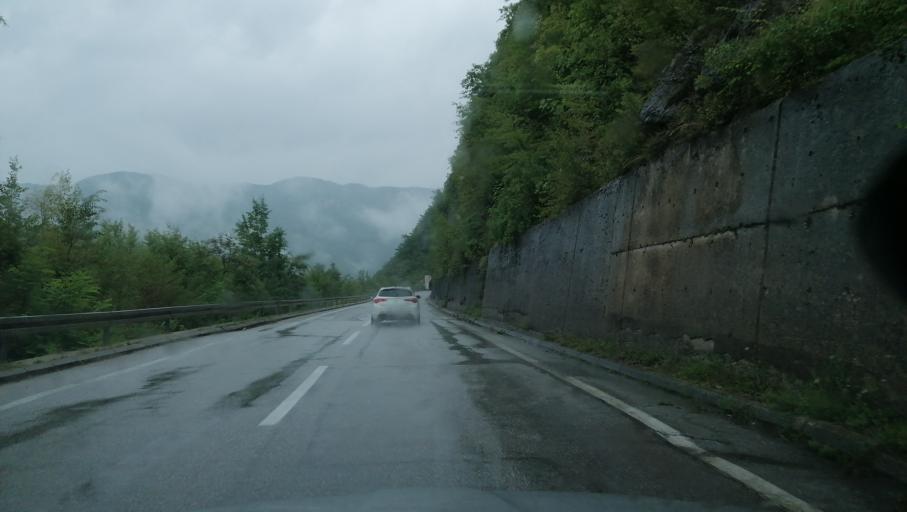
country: BA
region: Republika Srpska
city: Visegrad
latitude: 43.7110
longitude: 19.1692
